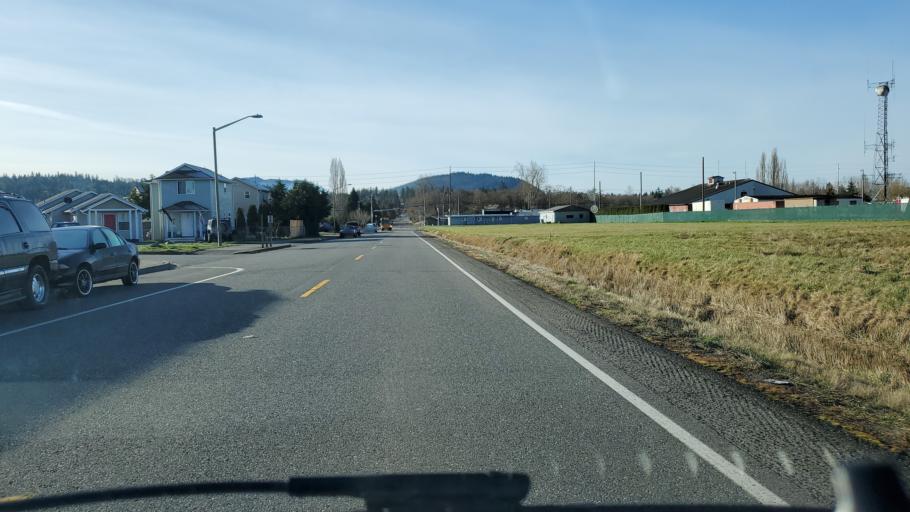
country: US
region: Washington
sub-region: Skagit County
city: Mount Vernon
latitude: 48.4379
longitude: -122.3026
